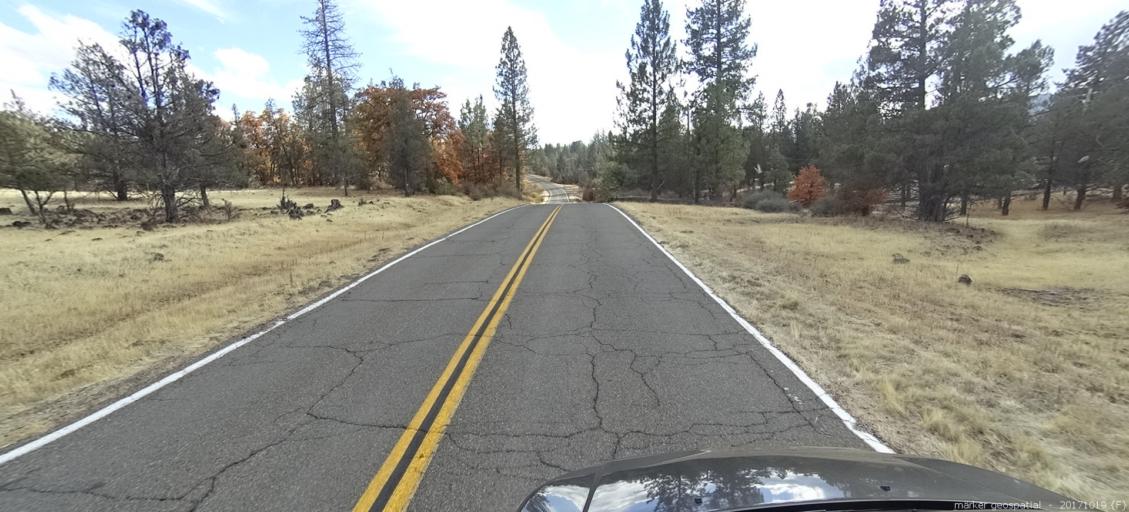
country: US
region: California
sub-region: Shasta County
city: Burney
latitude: 40.9793
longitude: -121.4333
